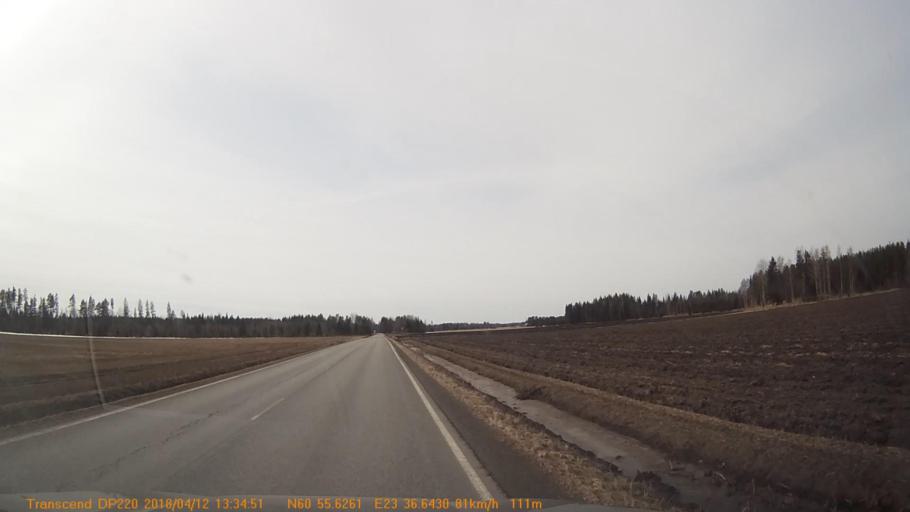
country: FI
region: Haeme
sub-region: Forssa
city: Forssa
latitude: 60.9271
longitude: 23.6104
